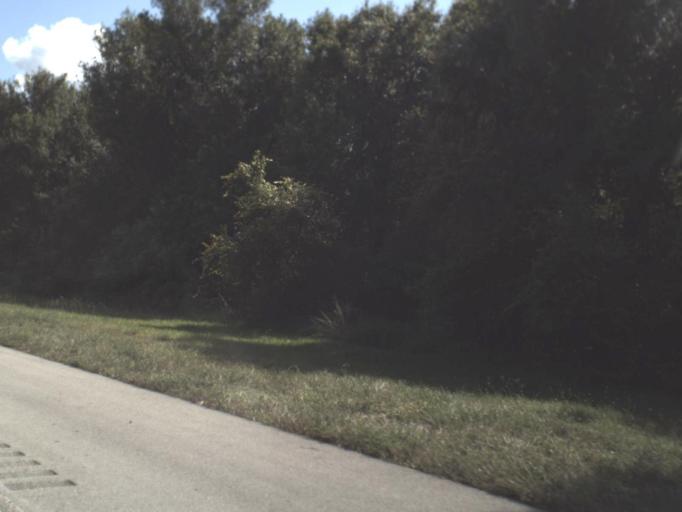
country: US
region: Florida
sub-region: Osceola County
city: Saint Cloud
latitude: 28.0565
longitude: -81.2289
